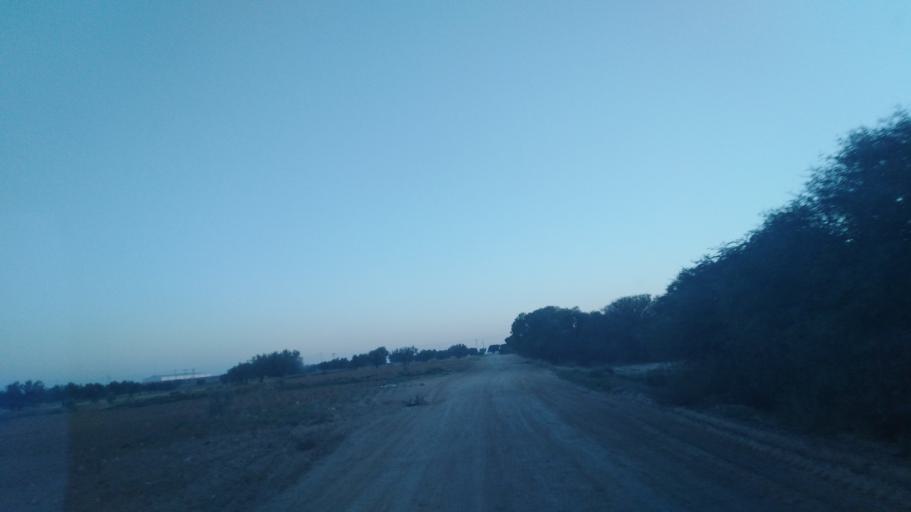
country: TN
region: Safaqis
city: Sfax
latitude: 34.7282
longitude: 10.4463
